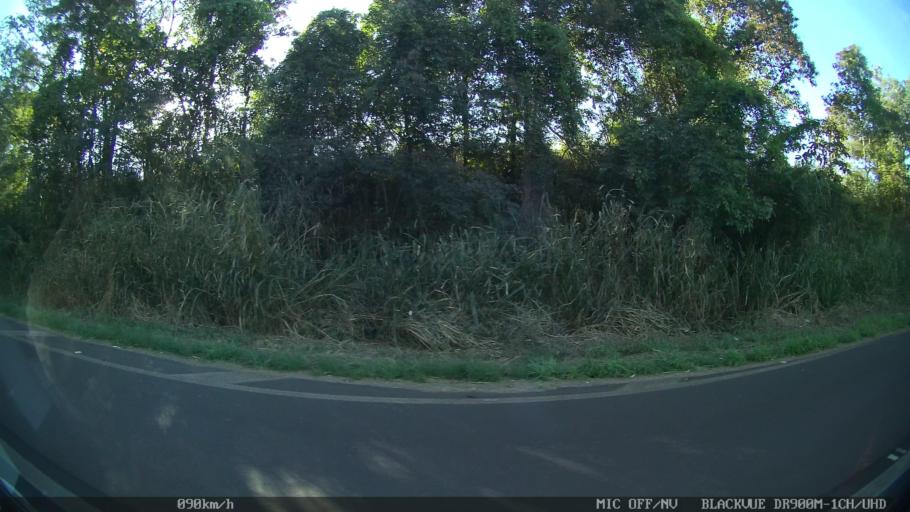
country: BR
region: Sao Paulo
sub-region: Guapiacu
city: Guapiacu
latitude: -20.7567
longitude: -49.1602
